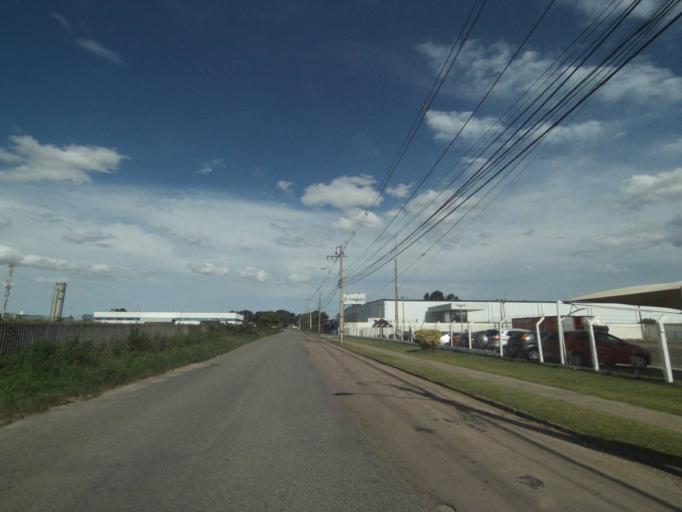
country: BR
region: Parana
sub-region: Curitiba
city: Curitiba
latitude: -25.5039
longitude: -49.3339
